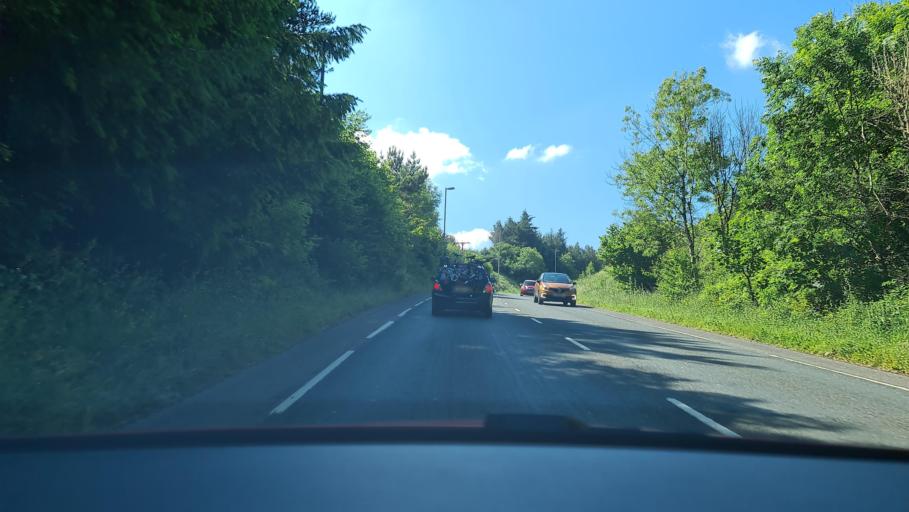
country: GB
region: England
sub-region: Cornwall
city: Liskeard
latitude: 50.4537
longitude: -4.4496
